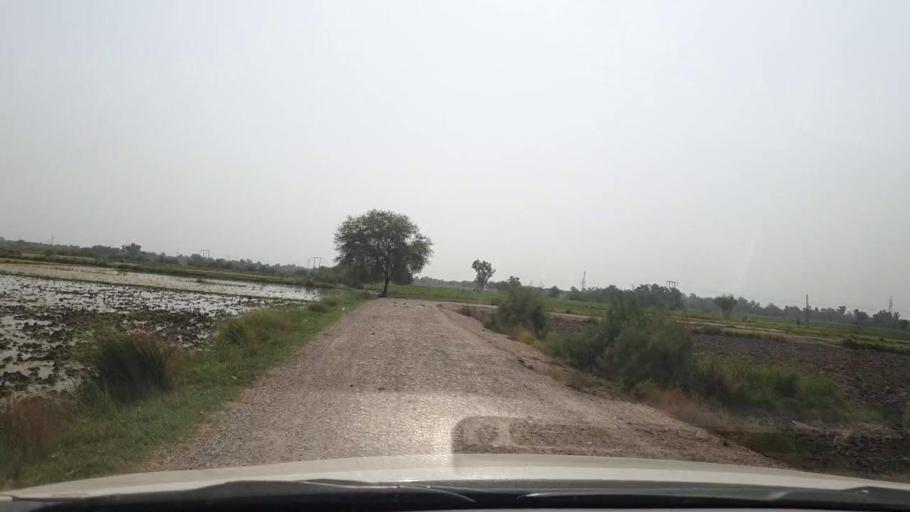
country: PK
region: Sindh
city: Shikarpur
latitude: 27.9818
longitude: 68.6734
